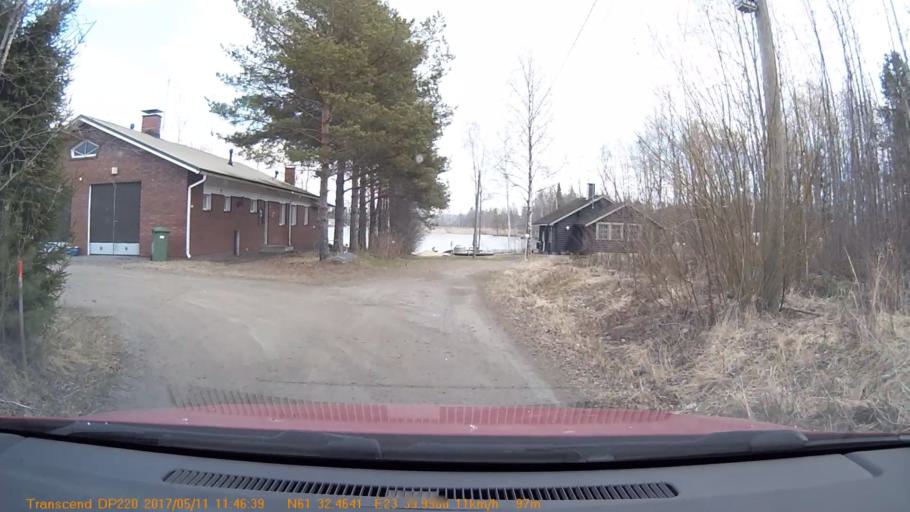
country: FI
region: Pirkanmaa
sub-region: Tampere
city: Yloejaervi
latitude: 61.5411
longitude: 23.6668
